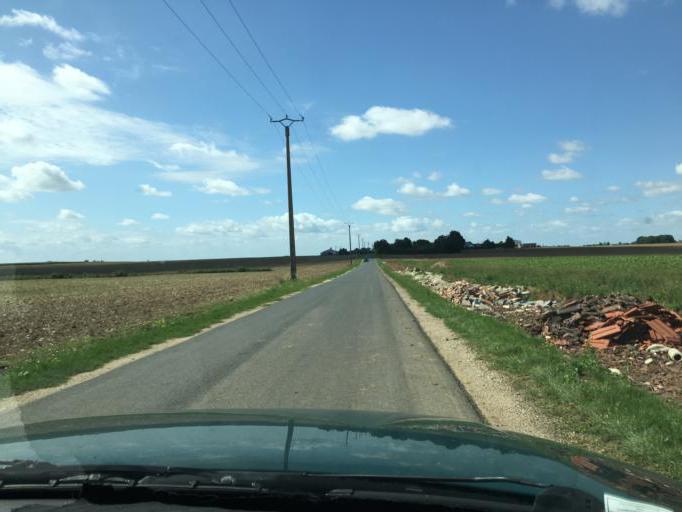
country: FR
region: Centre
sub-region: Departement du Loiret
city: Bricy
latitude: 48.0048
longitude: 1.7328
